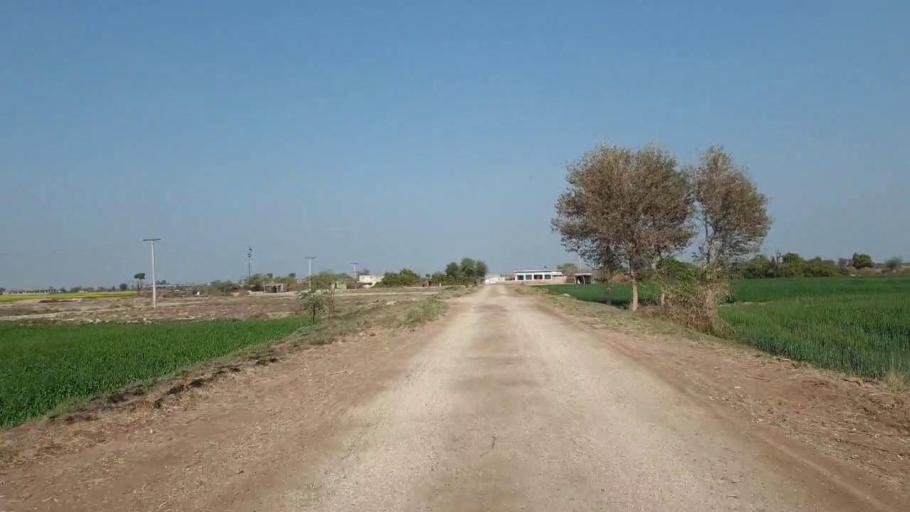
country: PK
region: Sindh
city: Hala
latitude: 25.9462
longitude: 68.4337
